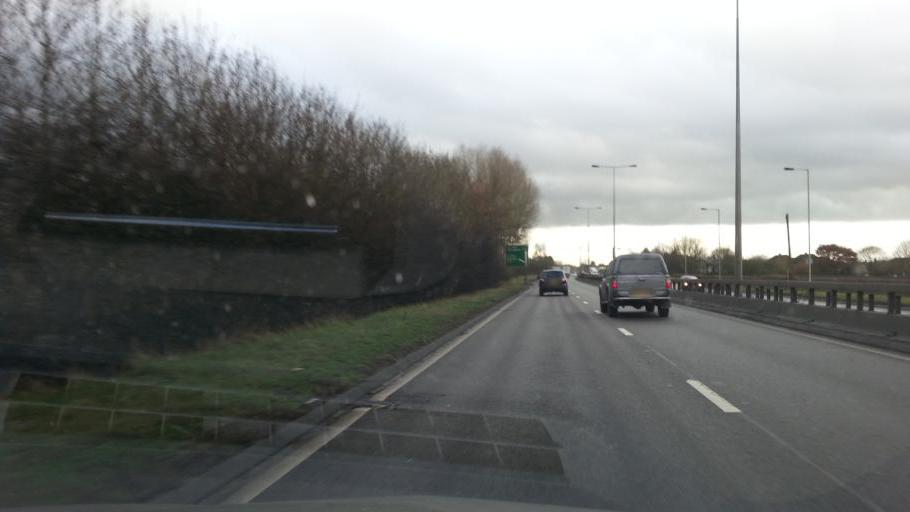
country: GB
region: England
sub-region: Staffordshire
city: Alrewas
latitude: 52.7350
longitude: -1.7357
